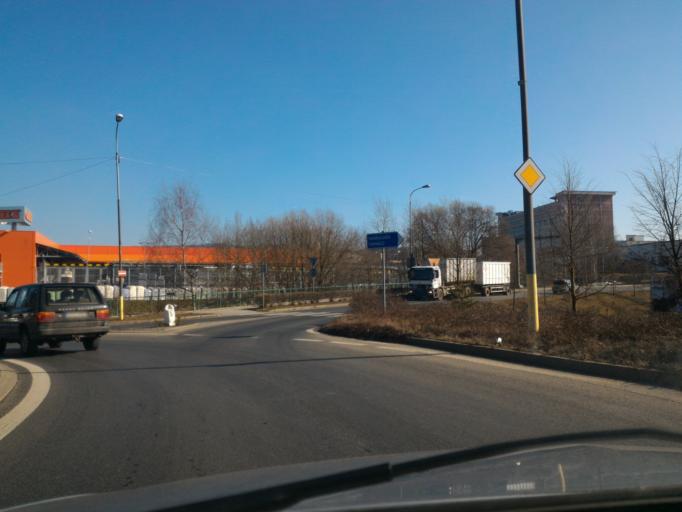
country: CZ
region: Liberecky
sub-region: Okres Jablonec nad Nisou
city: Jablonec nad Nisou
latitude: 50.7331
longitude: 15.1581
